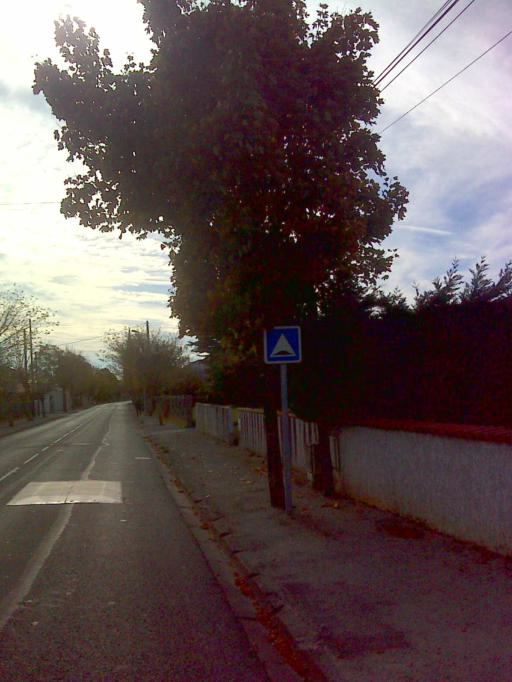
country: FR
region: Poitou-Charentes
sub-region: Departement de la Charente-Maritime
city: Marennes
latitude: 45.8270
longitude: -1.1018
